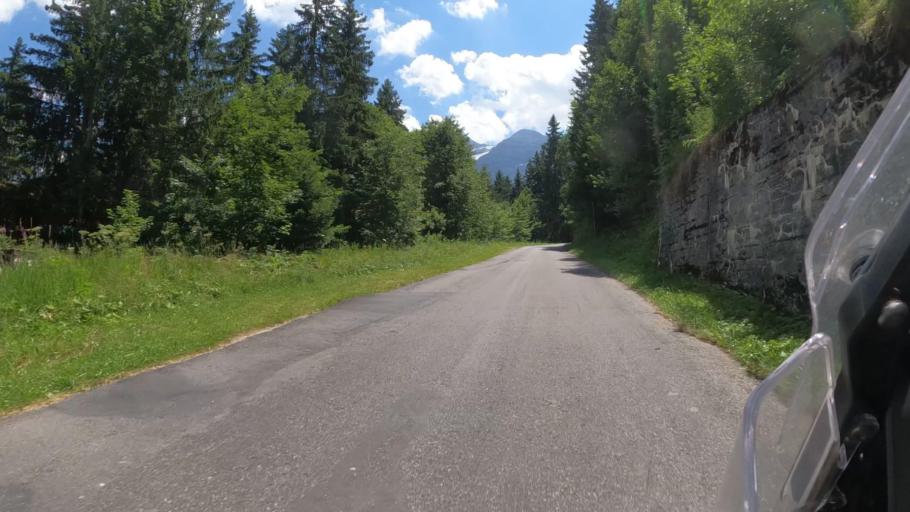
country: CH
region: Vaud
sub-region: Aigle District
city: Villars-sur-Ollon
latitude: 46.3437
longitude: 7.1474
